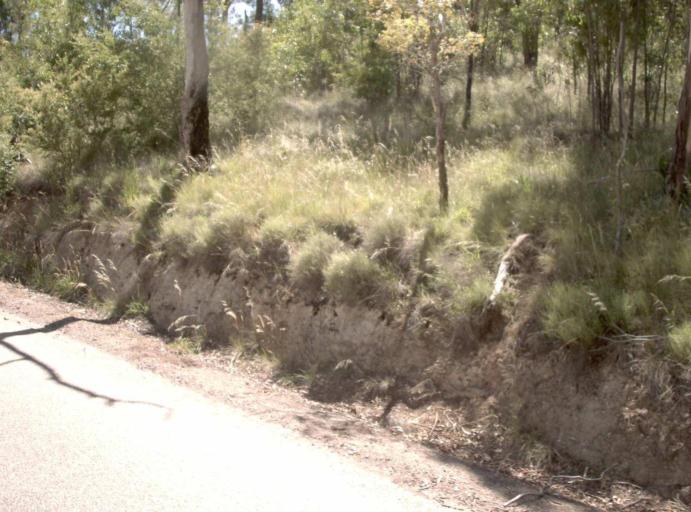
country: AU
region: Victoria
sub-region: East Gippsland
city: Lakes Entrance
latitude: -37.4625
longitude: 148.1953
